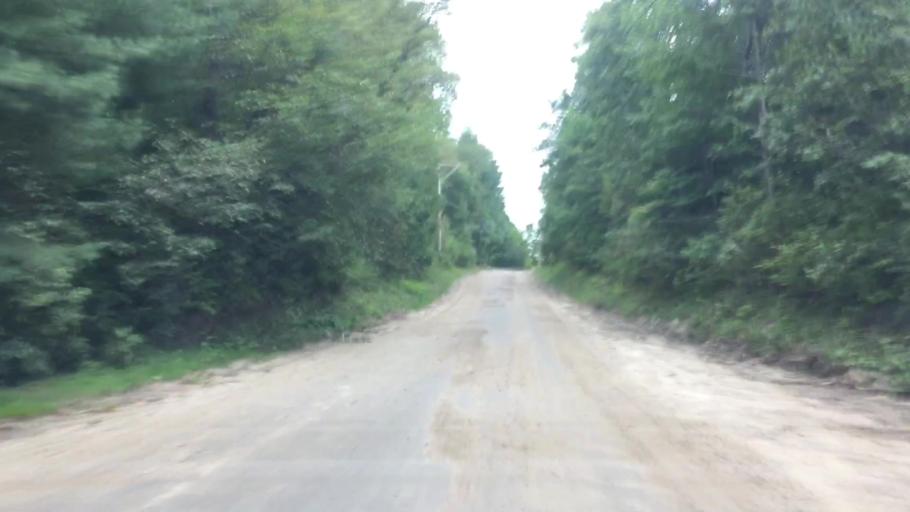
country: US
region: Maine
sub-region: Cumberland County
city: New Gloucester
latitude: 43.9067
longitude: -70.2353
